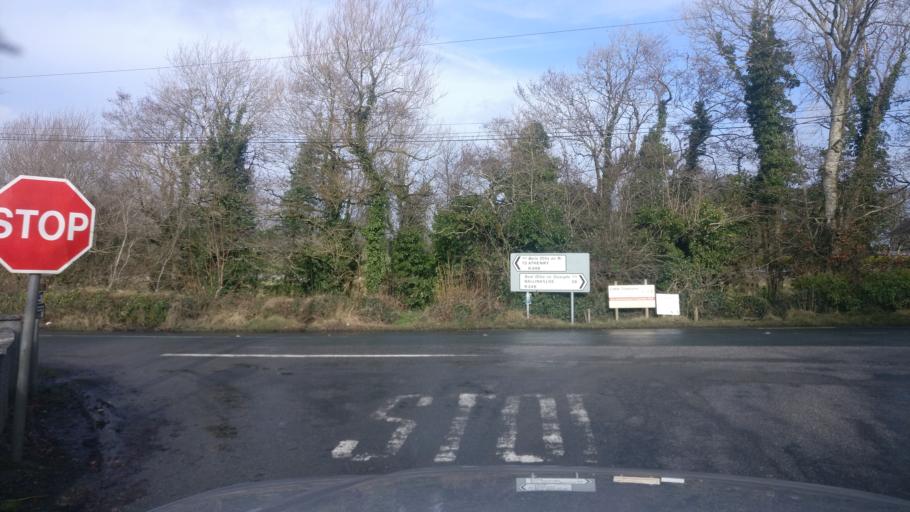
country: IE
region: Connaught
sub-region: County Galway
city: Loughrea
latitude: 53.2834
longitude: -8.5853
